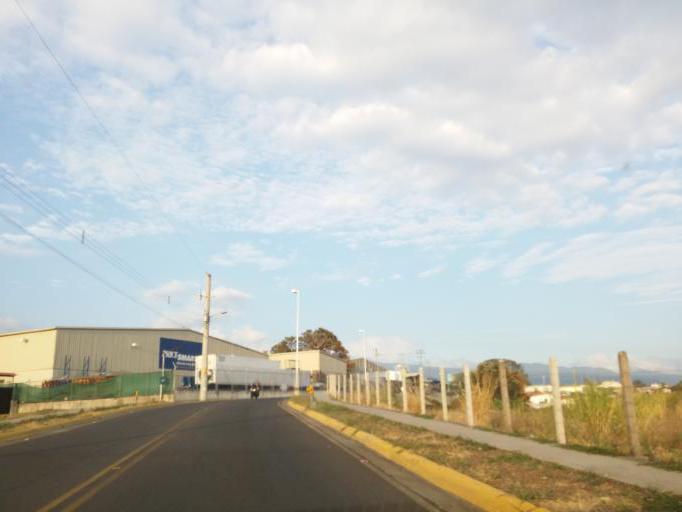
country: CR
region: Alajuela
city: Alajuela
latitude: 10.0110
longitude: -84.2237
